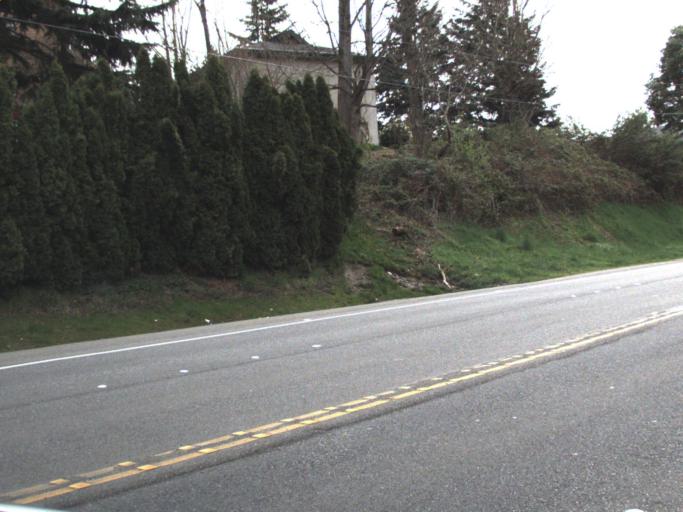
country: US
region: Washington
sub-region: King County
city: Normandy Park
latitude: 47.4461
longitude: -122.3302
